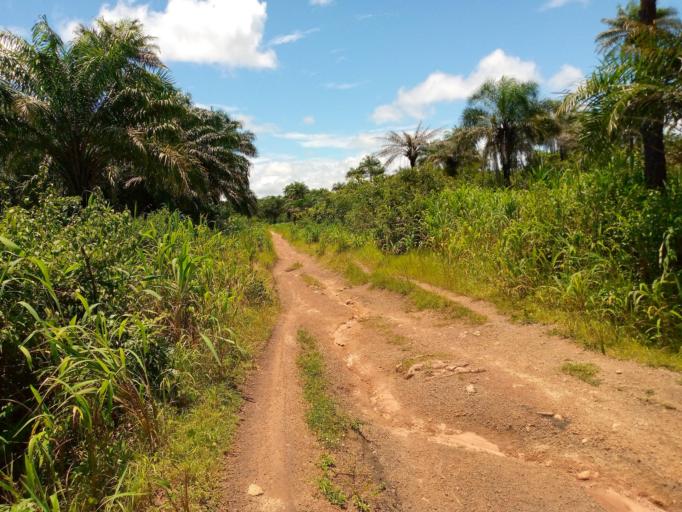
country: SL
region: Northern Province
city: Makeni
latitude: 9.0506
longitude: -12.1552
